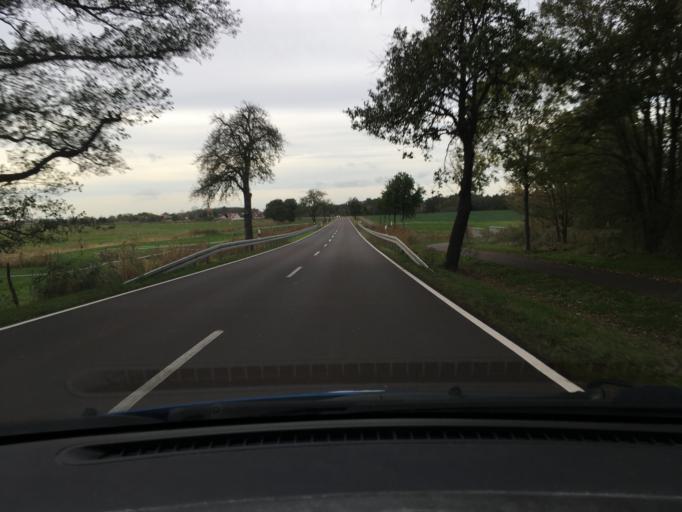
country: DE
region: Saxony-Anhalt
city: Wahlitz
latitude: 52.1105
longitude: 11.7788
